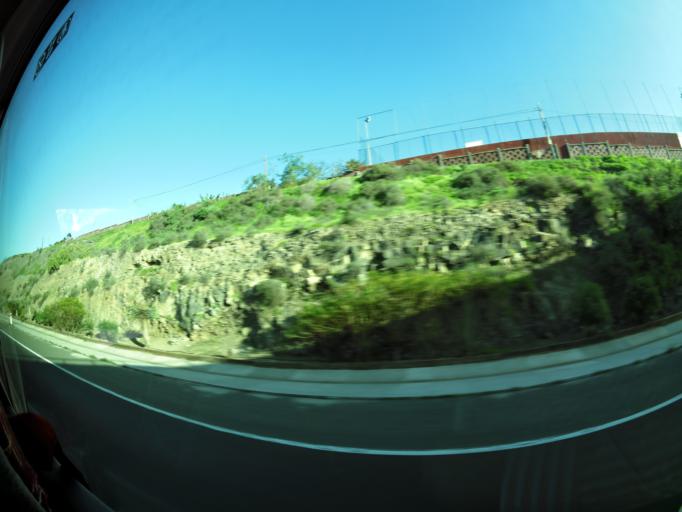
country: ES
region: Canary Islands
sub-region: Provincia de Las Palmas
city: Galdar
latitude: 28.1301
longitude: -15.6571
